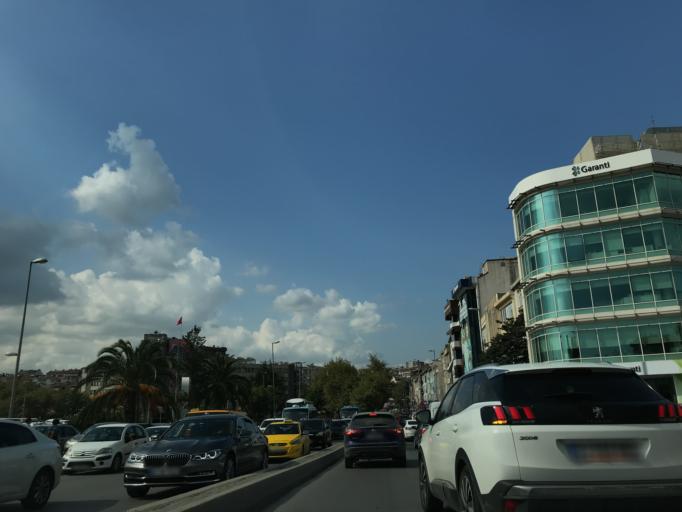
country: TR
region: Istanbul
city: UEskuedar
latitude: 40.9916
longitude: 29.0394
